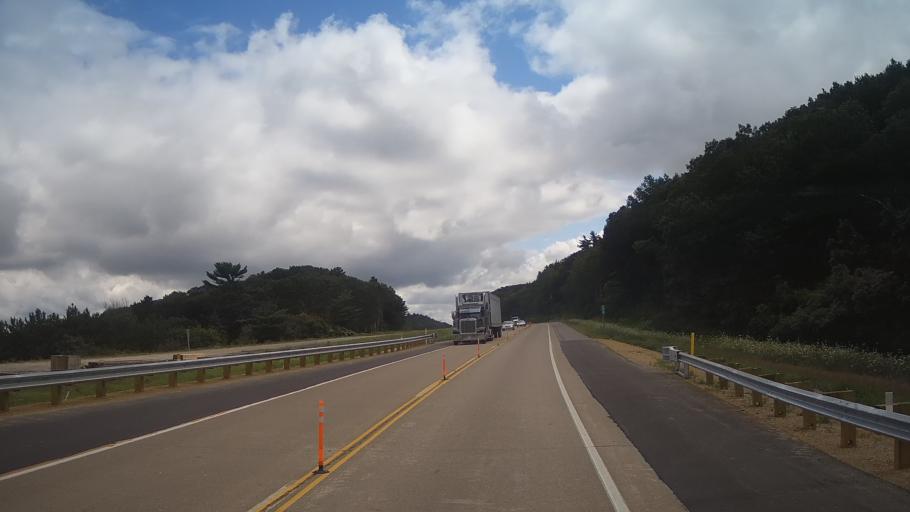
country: US
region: Wisconsin
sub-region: Monroe County
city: Tomah
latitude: 43.9518
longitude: -90.5369
